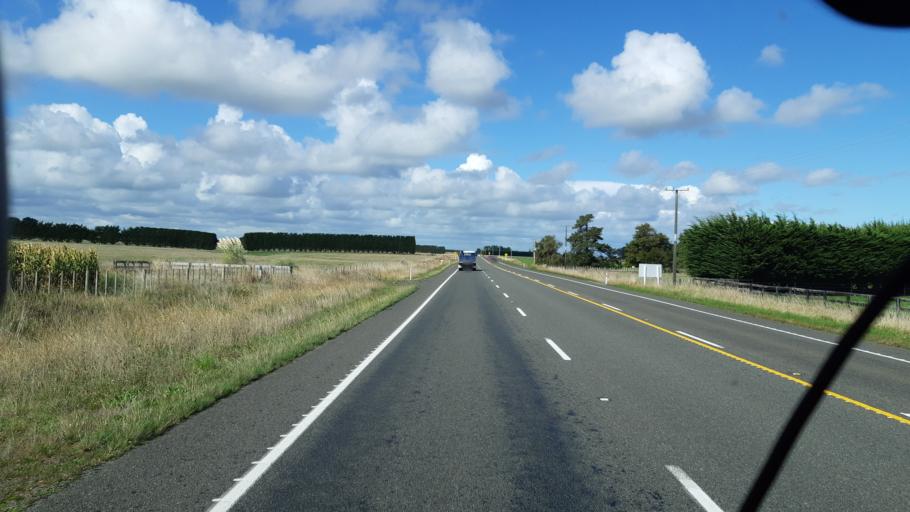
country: NZ
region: Manawatu-Wanganui
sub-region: Wanganui District
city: Wanganui
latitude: -39.9832
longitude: 175.1517
